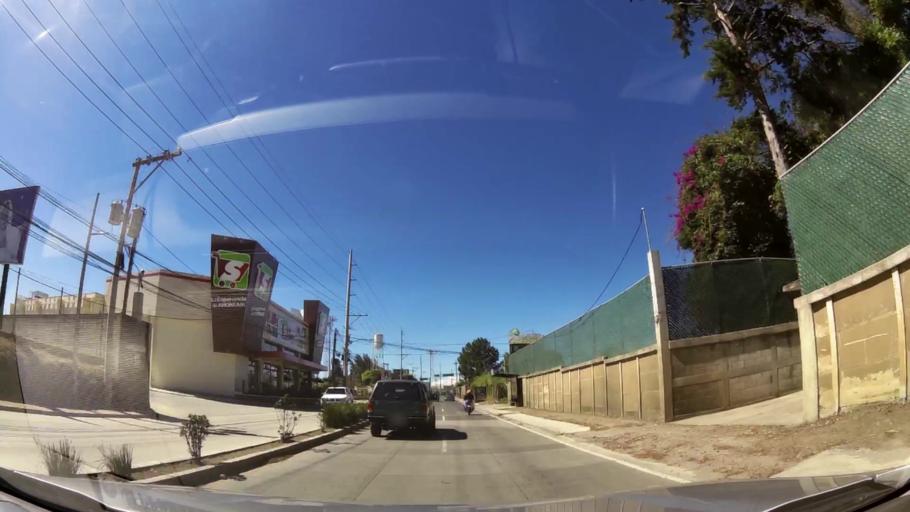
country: GT
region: Guatemala
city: San Jose Pinula
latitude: 14.5442
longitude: -90.4317
